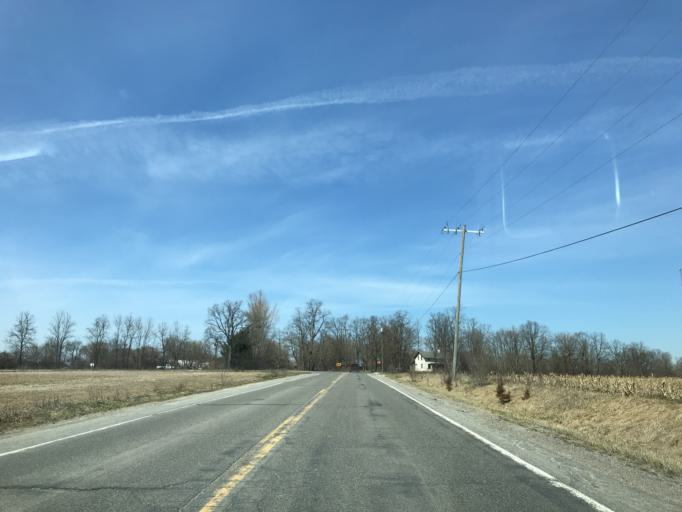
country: US
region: Michigan
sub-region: Washtenaw County
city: Ann Arbor
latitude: 42.3414
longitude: -83.7085
